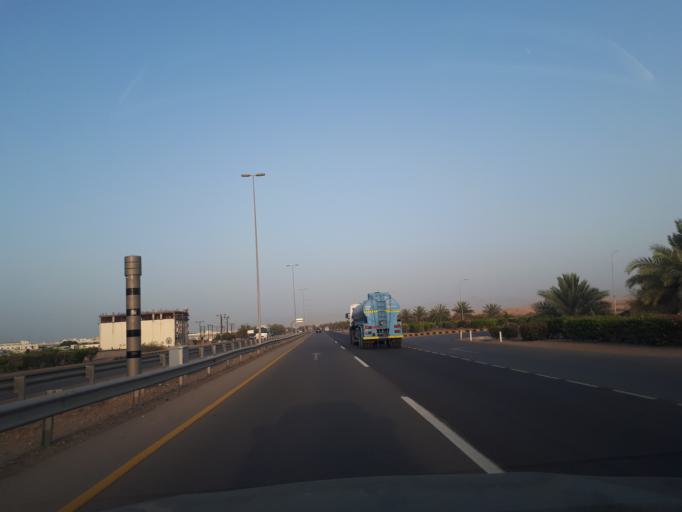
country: OM
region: Muhafazat Masqat
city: As Sib al Jadidah
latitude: 23.5904
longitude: 58.2167
